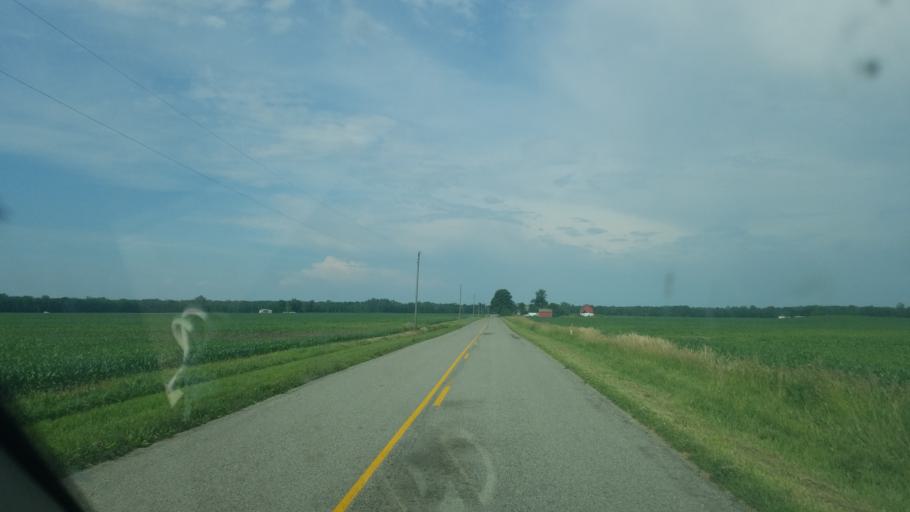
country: US
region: Ohio
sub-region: Champaign County
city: North Lewisburg
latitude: 40.1822
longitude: -83.4687
